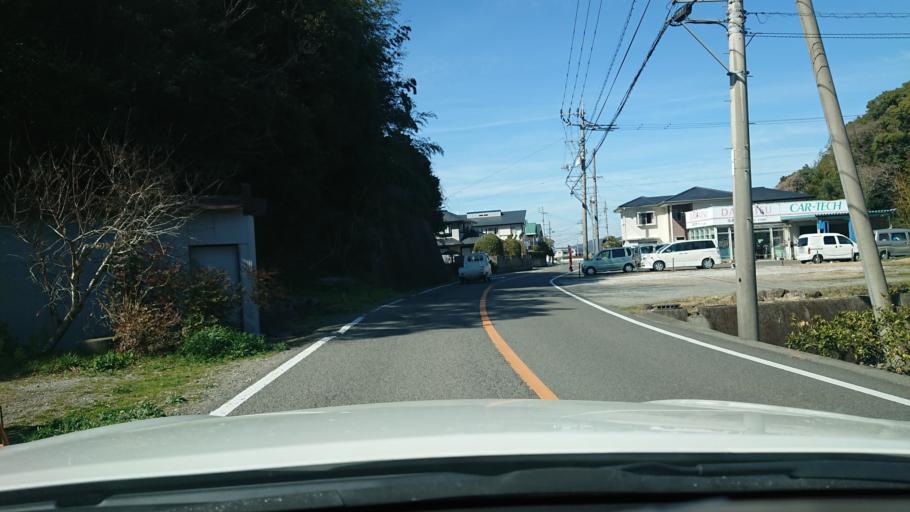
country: JP
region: Tokushima
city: Komatsushimacho
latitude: 33.9739
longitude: 134.5910
